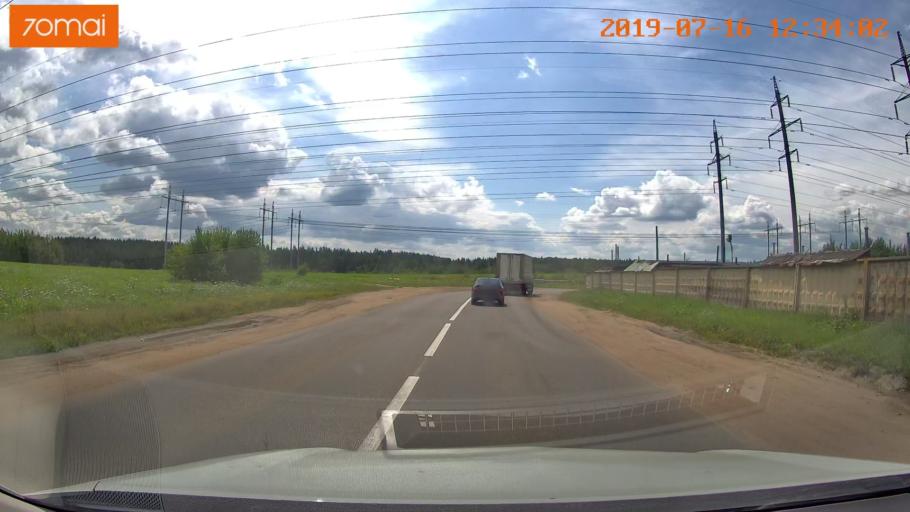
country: BY
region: Minsk
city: Malinovka
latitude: 53.8687
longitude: 27.4103
